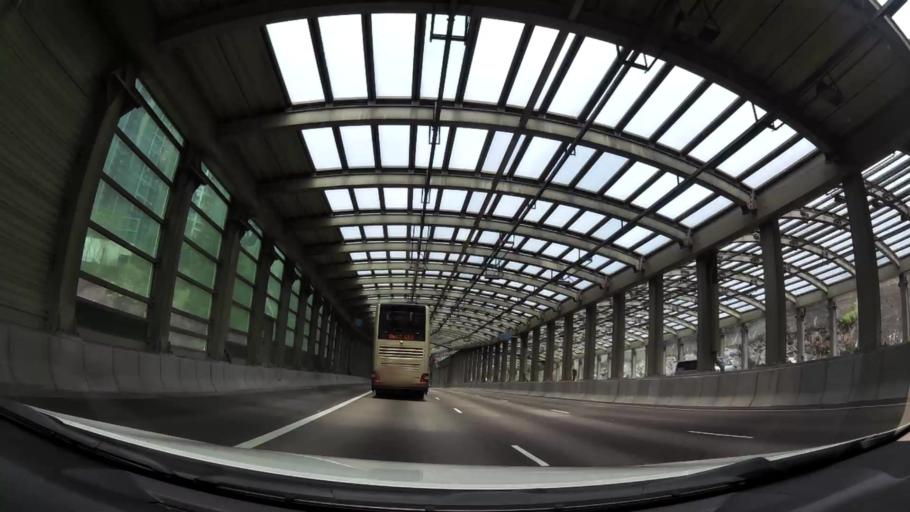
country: HK
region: Tuen Mun
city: Tuen Mun
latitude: 22.3807
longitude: 113.9829
